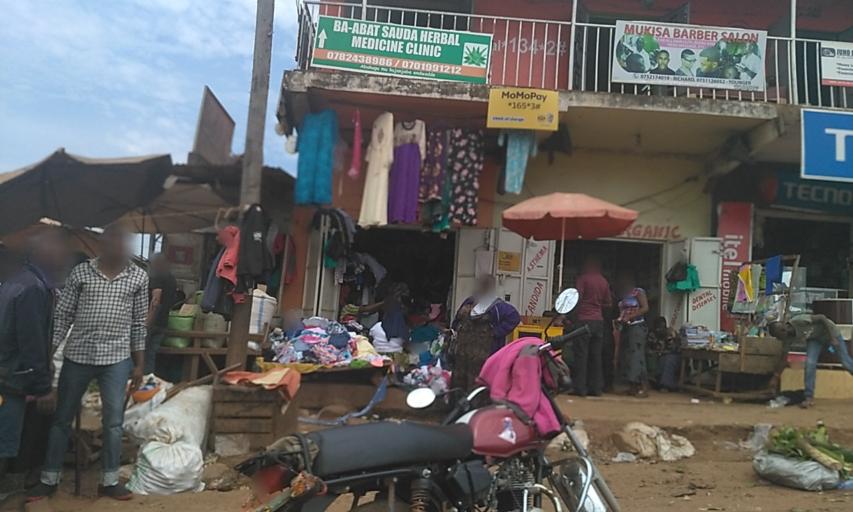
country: UG
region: Central Region
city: Kampala Central Division
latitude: 0.2999
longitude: 32.5336
